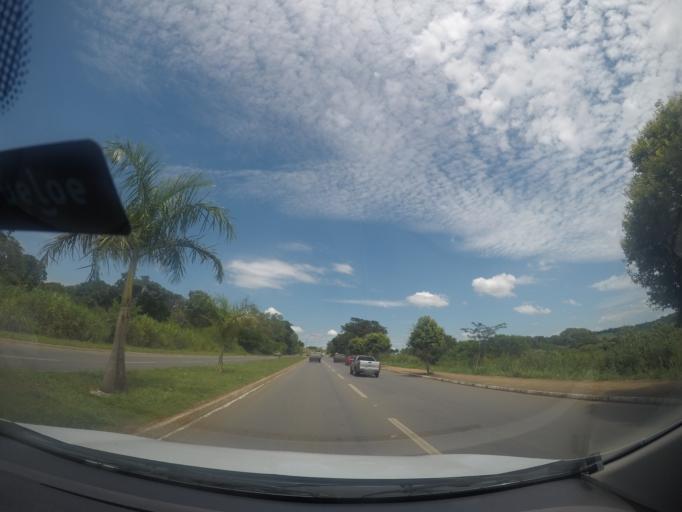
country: BR
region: Goias
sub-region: Goiania
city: Goiania
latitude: -16.6835
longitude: -49.3374
